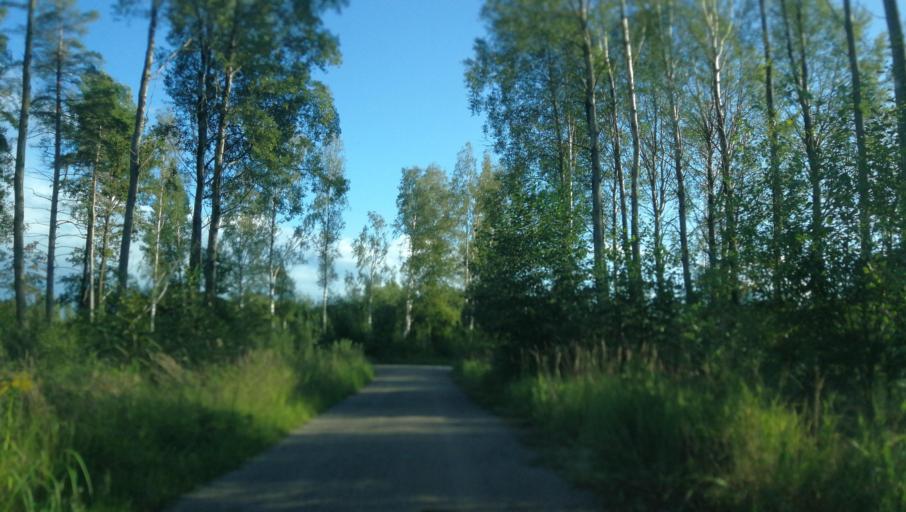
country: LV
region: Valmieras Rajons
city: Valmiera
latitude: 57.5299
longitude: 25.4637
